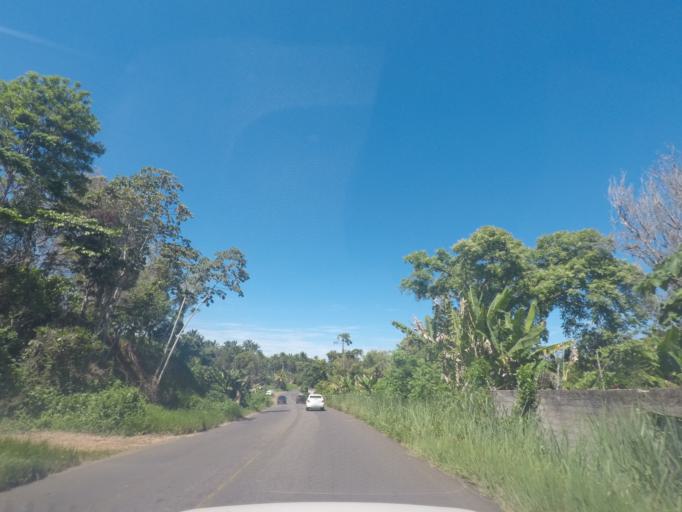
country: BR
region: Bahia
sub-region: Valenca
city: Valenca
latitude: -13.4450
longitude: -39.0827
